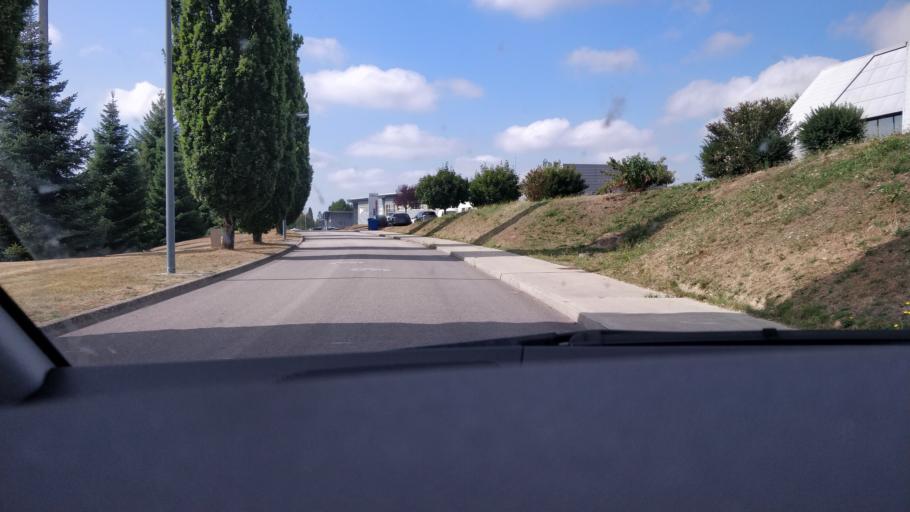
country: FR
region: Limousin
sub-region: Departement de la Haute-Vienne
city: Le Palais-sur-Vienne
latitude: 45.8638
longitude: 1.2916
